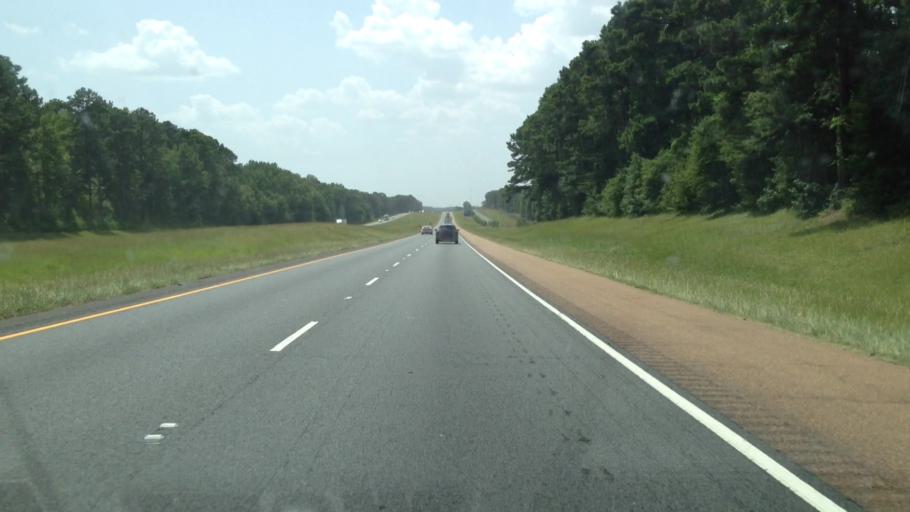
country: US
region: Louisiana
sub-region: Bienville Parish
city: Arcadia
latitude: 32.5595
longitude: -92.8906
